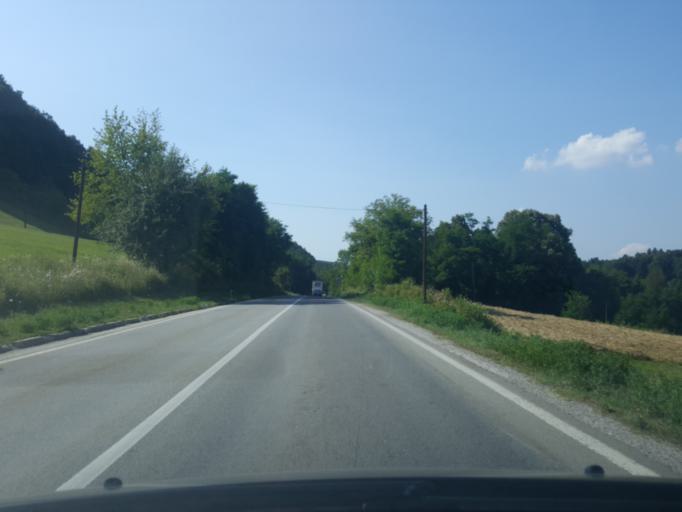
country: RS
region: Central Serbia
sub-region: Moravicki Okrug
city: Gornji Milanovac
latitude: 44.0732
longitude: 20.4888
